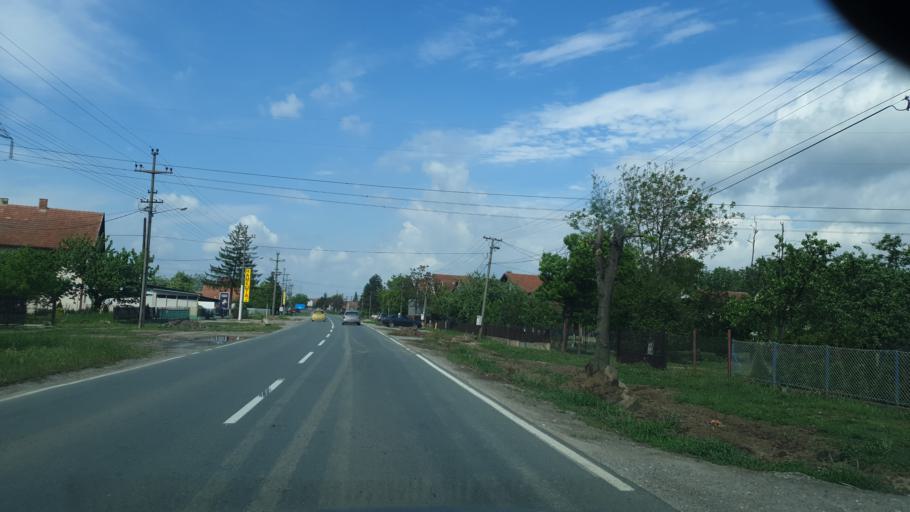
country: RS
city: Zvecka
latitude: 44.6291
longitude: 20.1794
